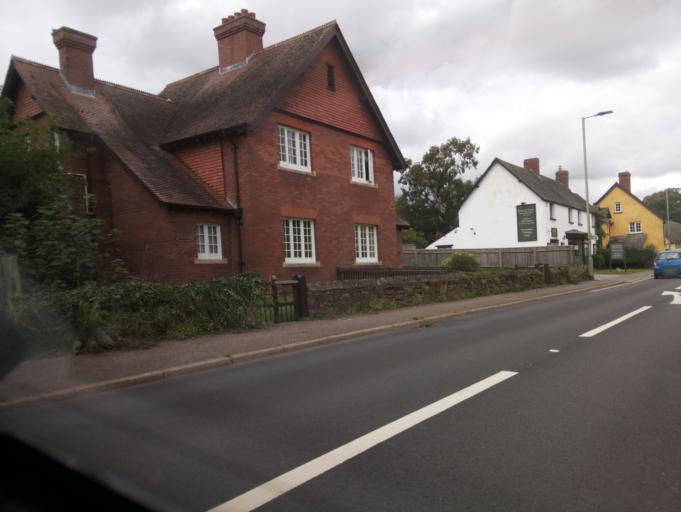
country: GB
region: England
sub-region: Devon
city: Heavitree
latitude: 50.7645
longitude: -3.4438
